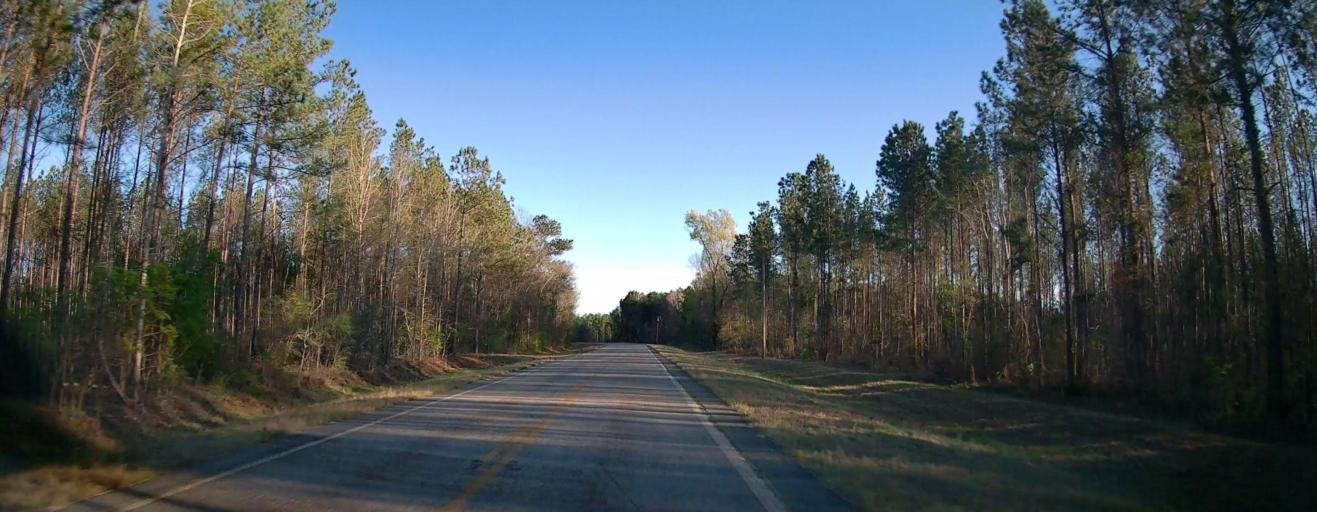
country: US
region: Georgia
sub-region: Wilcox County
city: Abbeville
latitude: 32.0727
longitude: -83.2840
